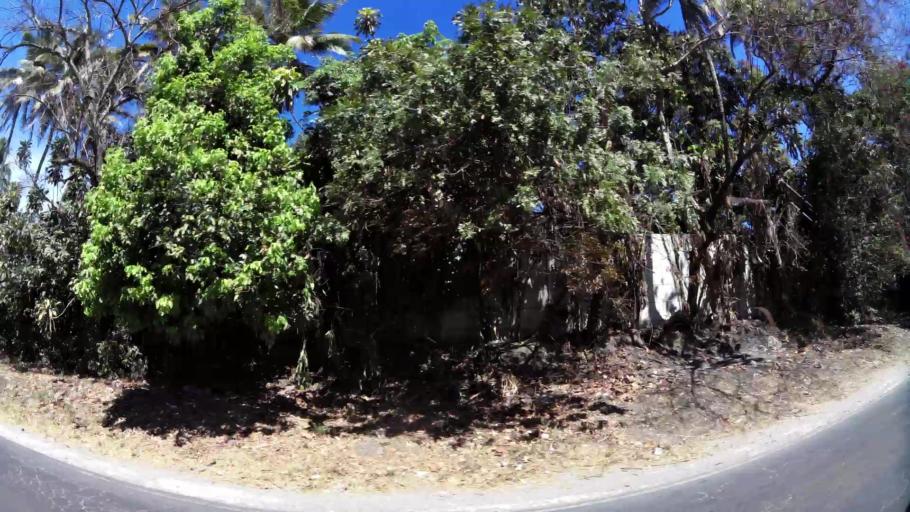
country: SV
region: San Salvador
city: Apopa
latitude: 13.8031
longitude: -89.1849
